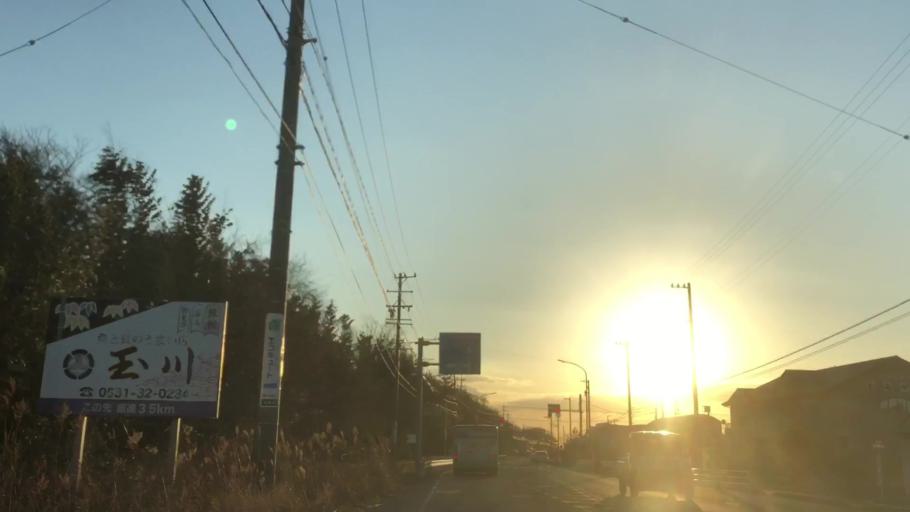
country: JP
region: Aichi
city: Tahara
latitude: 34.6419
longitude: 137.1399
